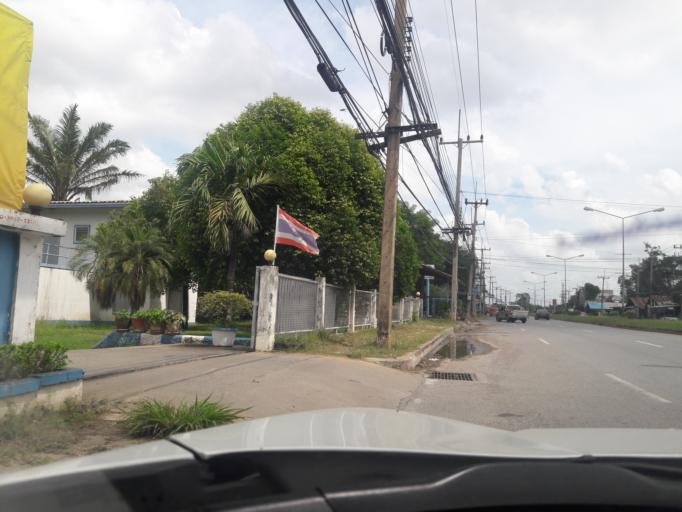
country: TH
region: Lop Buri
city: Ban Mi
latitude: 15.0445
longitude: 100.5475
